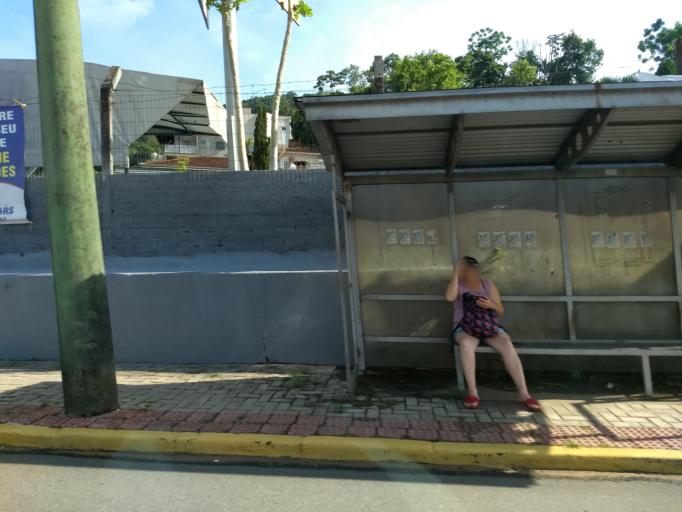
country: BR
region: Santa Catarina
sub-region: Jaragua Do Sul
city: Jaragua do Sul
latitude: -26.4718
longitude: -49.0891
